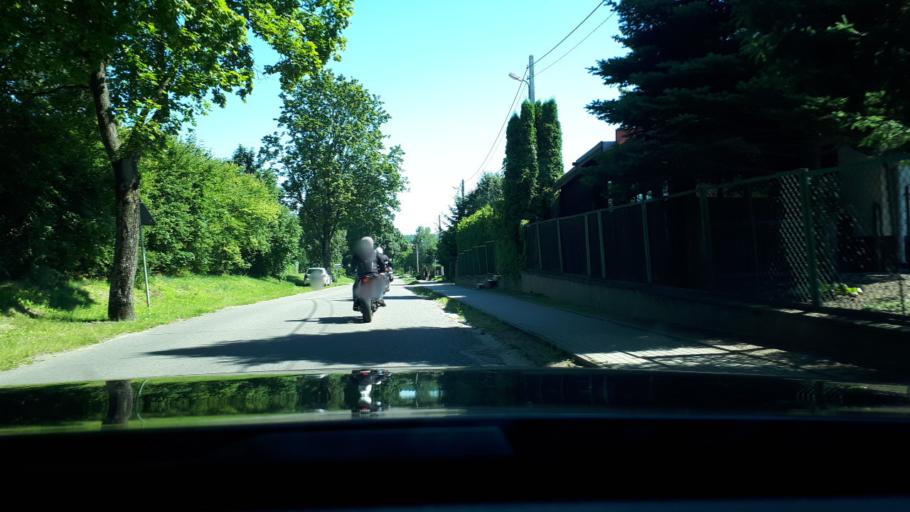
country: PL
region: Warmian-Masurian Voivodeship
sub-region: Powiat olsztynski
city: Stawiguda
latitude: 53.6552
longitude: 20.4021
